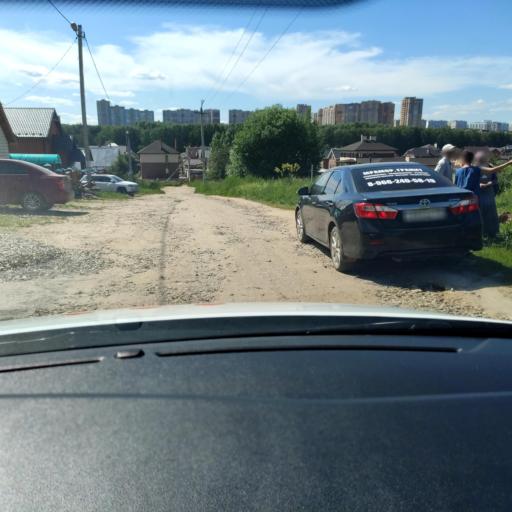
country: RU
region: Tatarstan
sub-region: Gorod Kazan'
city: Kazan
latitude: 55.7776
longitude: 49.2578
